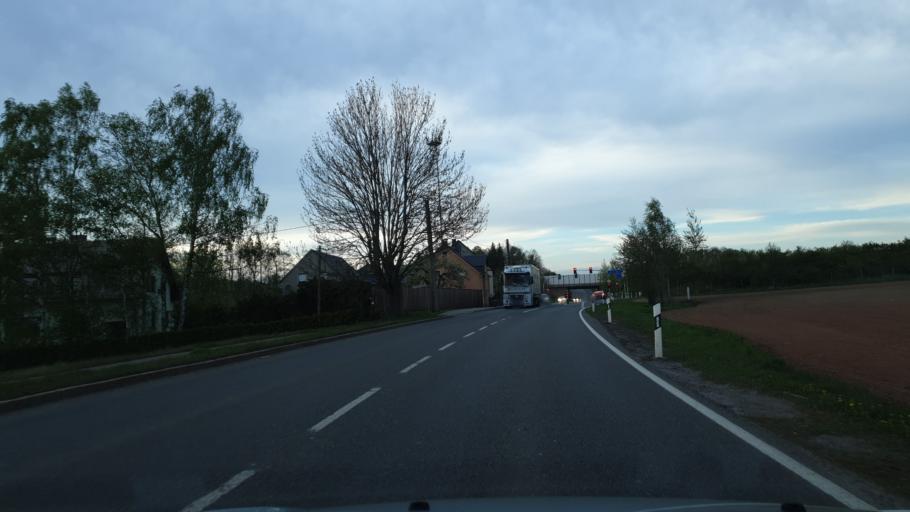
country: DE
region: Saxony
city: Oelsnitz
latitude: 50.6889
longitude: 12.6992
